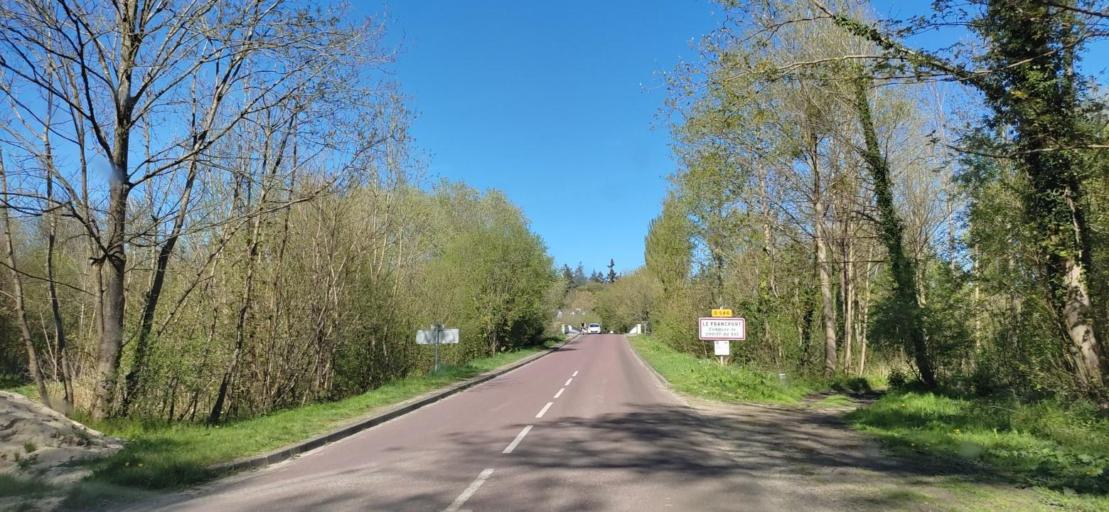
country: FR
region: Picardie
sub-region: Departement de l'Oise
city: Choisy-au-Bac
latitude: 49.4326
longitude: 2.9103
